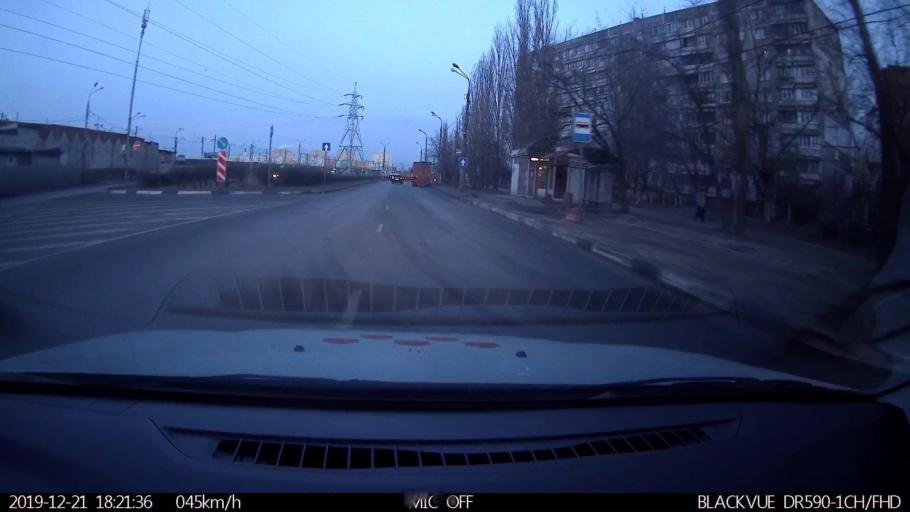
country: RU
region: Nizjnij Novgorod
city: Nizhniy Novgorod
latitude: 56.3366
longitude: 43.9271
